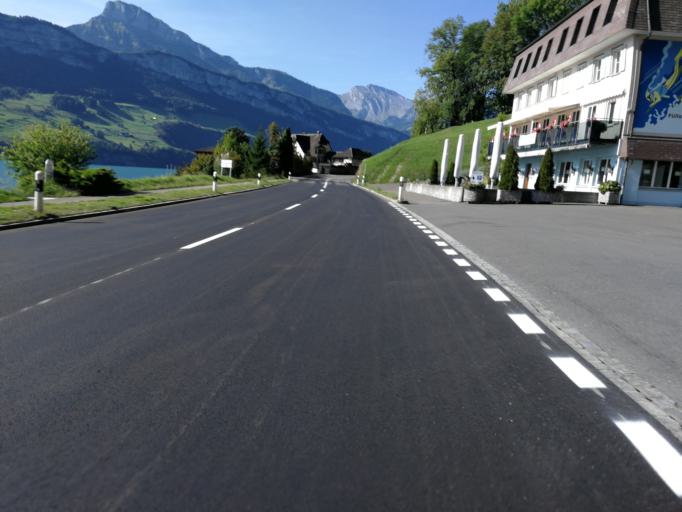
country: CH
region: Schwyz
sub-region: Bezirk Gersau
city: Gersau
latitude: 46.9979
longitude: 8.5697
